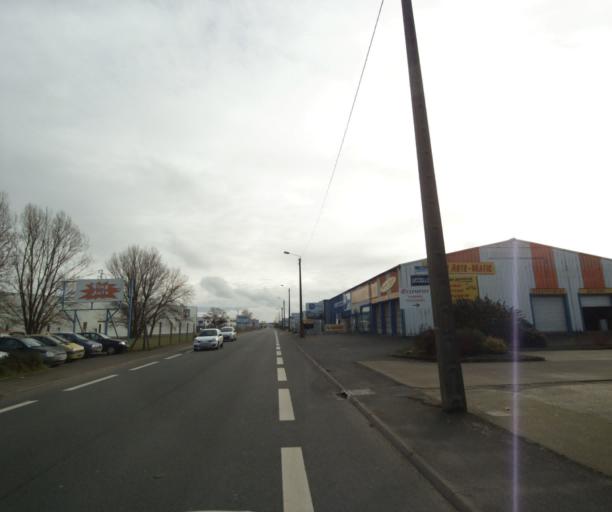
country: FR
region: Pays de la Loire
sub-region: Departement de la Sarthe
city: Allonnes
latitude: 47.9746
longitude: 0.1686
